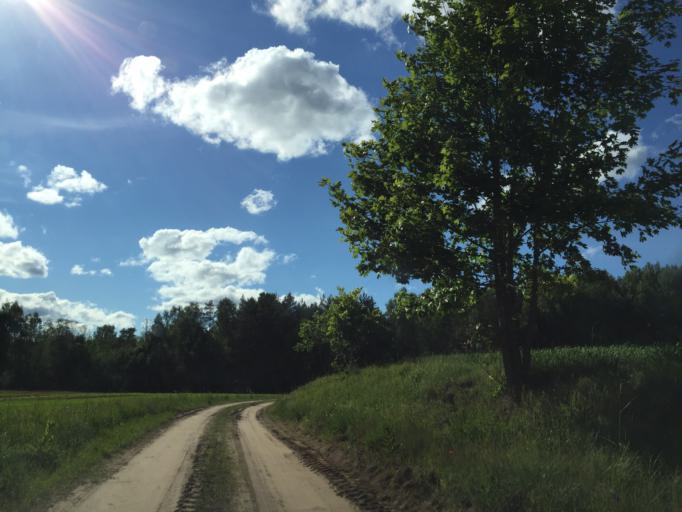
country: LV
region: Vecumnieki
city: Vecumnieki
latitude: 56.4398
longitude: 24.5879
